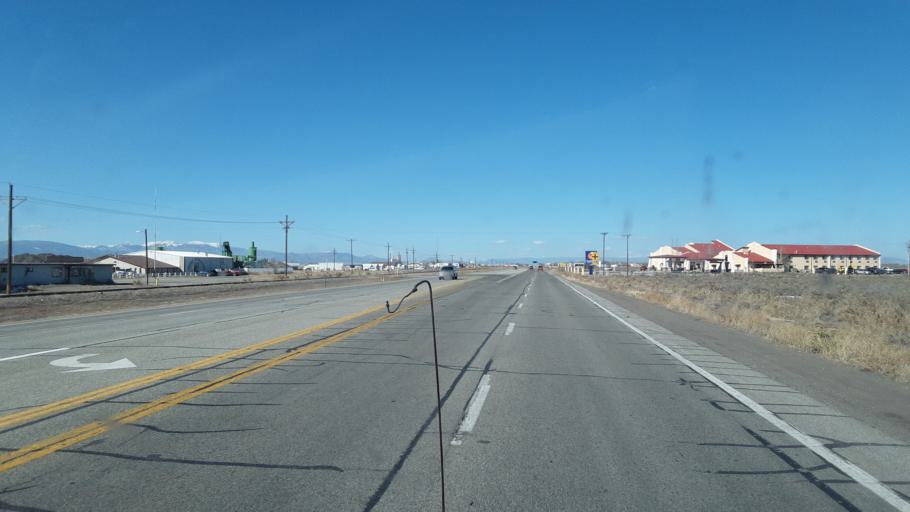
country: US
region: Colorado
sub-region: Alamosa County
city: Alamosa
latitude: 37.4820
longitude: -105.9104
